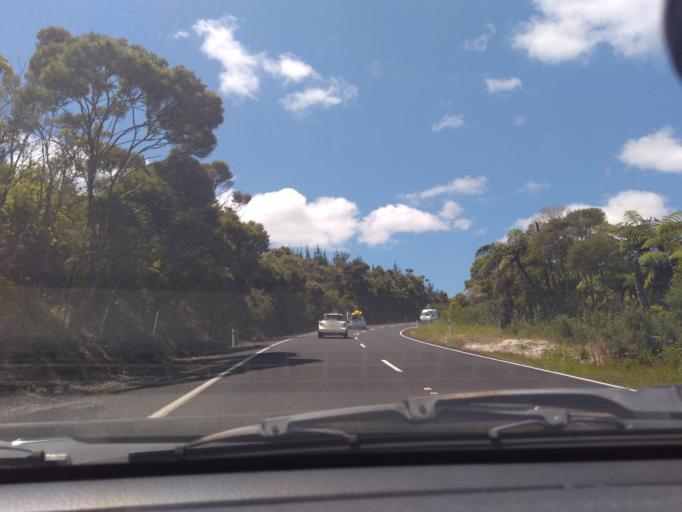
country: NZ
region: Northland
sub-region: Far North District
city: Kerikeri
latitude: -35.1209
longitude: 173.8489
